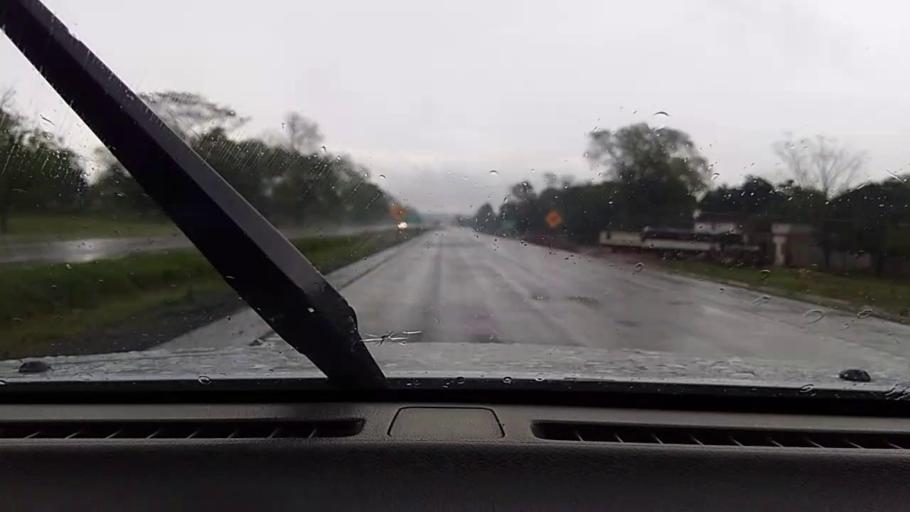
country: PY
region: Caaguazu
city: Repatriacion
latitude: -25.4589
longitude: -55.9204
